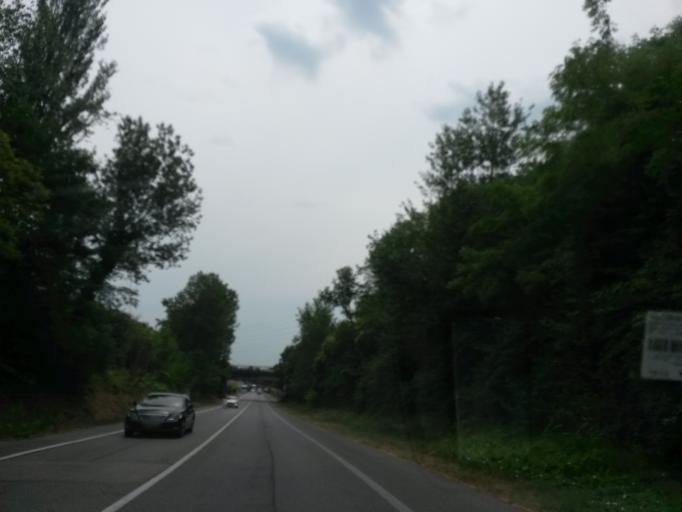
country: IT
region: Lombardy
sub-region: Provincia di Brescia
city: Desenzano del Garda
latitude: 45.4733
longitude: 10.5268
